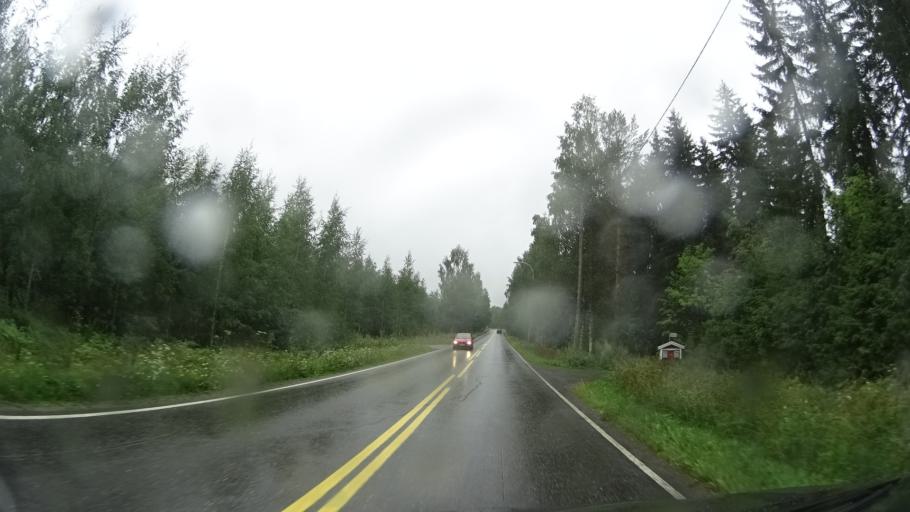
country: FI
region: North Karelia
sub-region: Keski-Karjala
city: Raeaekkylae
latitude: 62.3114
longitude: 29.5908
